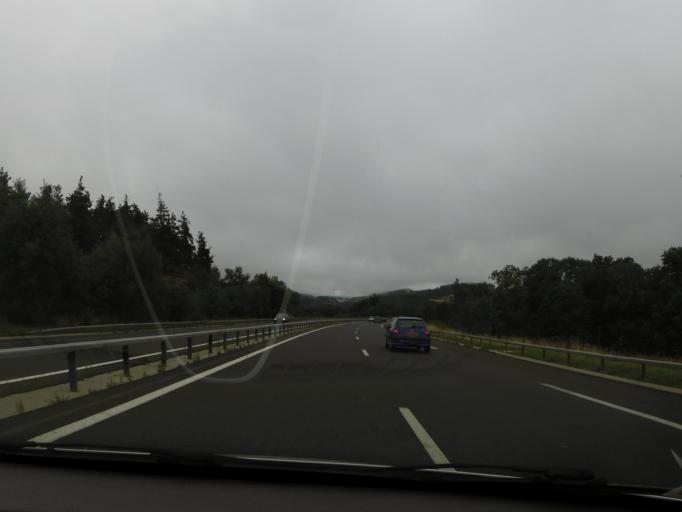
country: FR
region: Languedoc-Roussillon
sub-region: Departement de la Lozere
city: Marvejols
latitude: 44.6202
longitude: 3.2532
